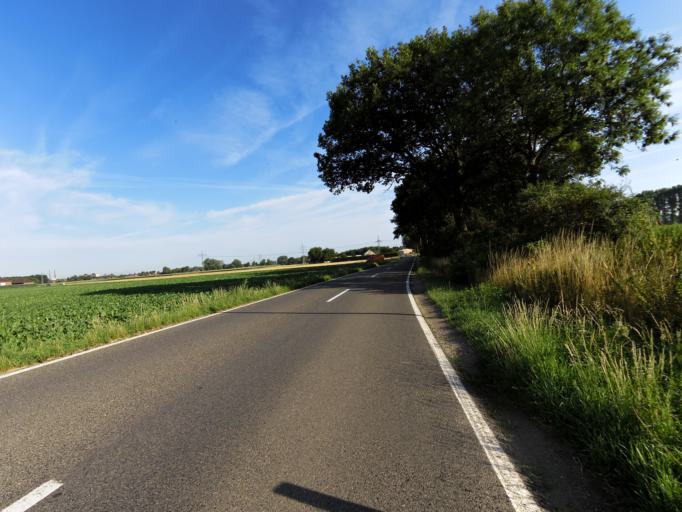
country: DE
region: North Rhine-Westphalia
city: Huckelhoven
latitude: 51.0498
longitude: 6.1738
